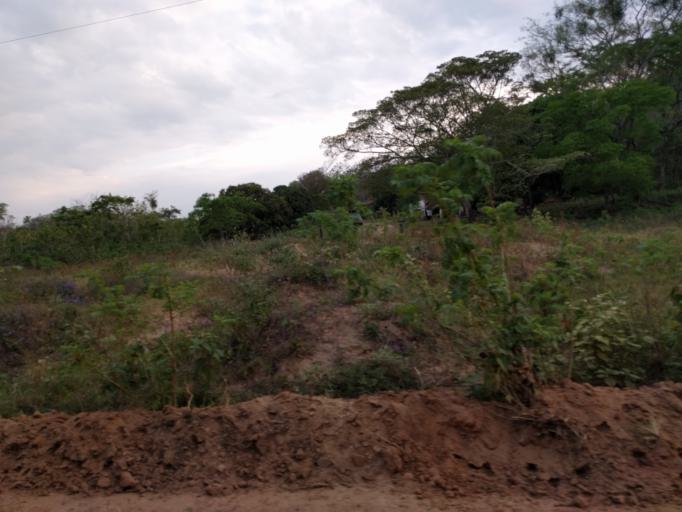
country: BO
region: Santa Cruz
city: Santa Rita
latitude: -17.9343
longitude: -63.3657
